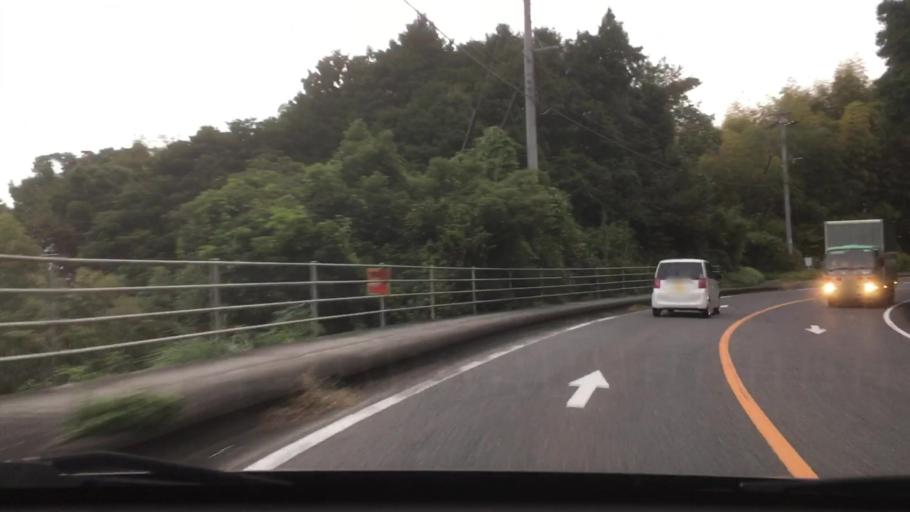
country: JP
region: Nagasaki
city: Sasebo
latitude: 33.0451
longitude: 129.7319
